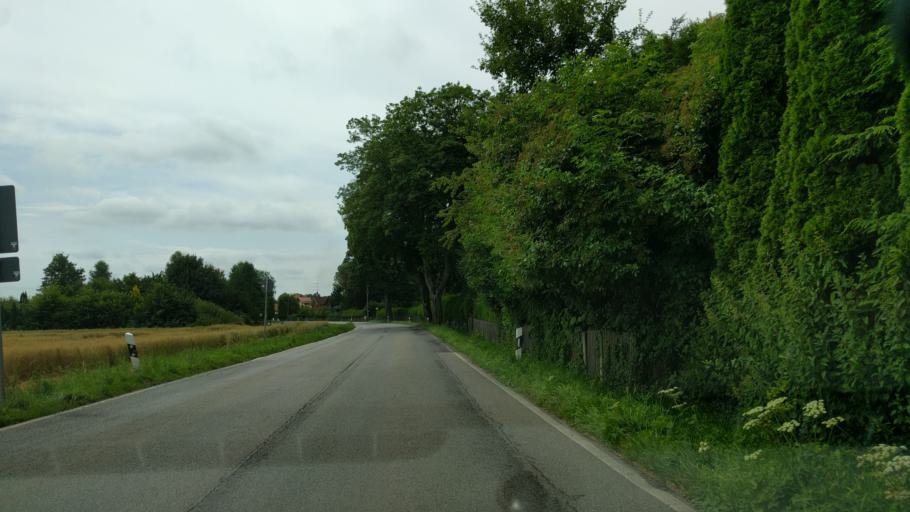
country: DE
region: Bavaria
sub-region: Upper Bavaria
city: Strasslach-Dingharting
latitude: 48.0097
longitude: 11.5149
